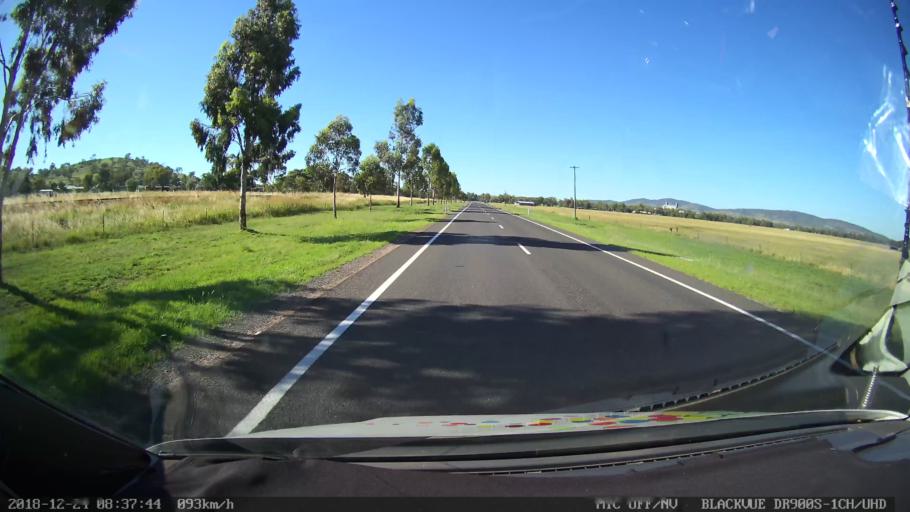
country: AU
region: New South Wales
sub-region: Liverpool Plains
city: Quirindi
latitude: -31.3331
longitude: 150.6483
